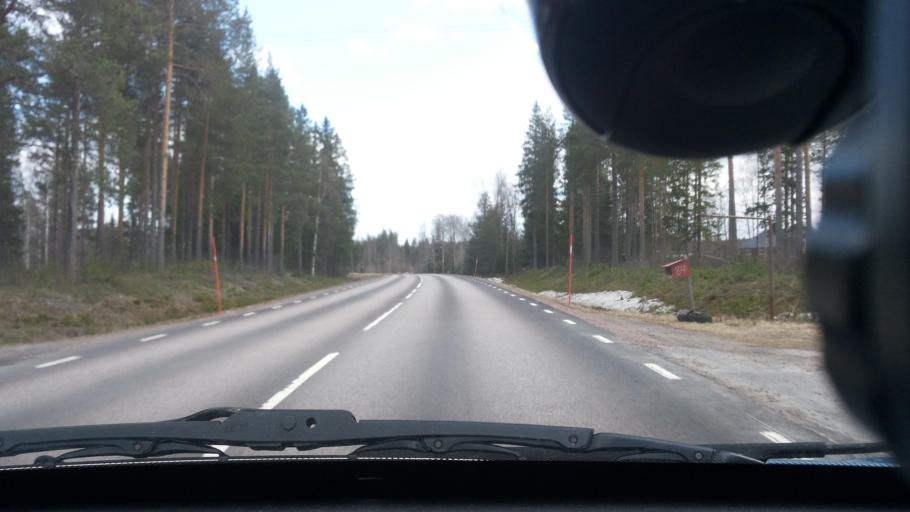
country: SE
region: Norrbotten
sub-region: Lulea Kommun
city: Sodra Sunderbyn
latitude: 65.6071
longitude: 21.9628
